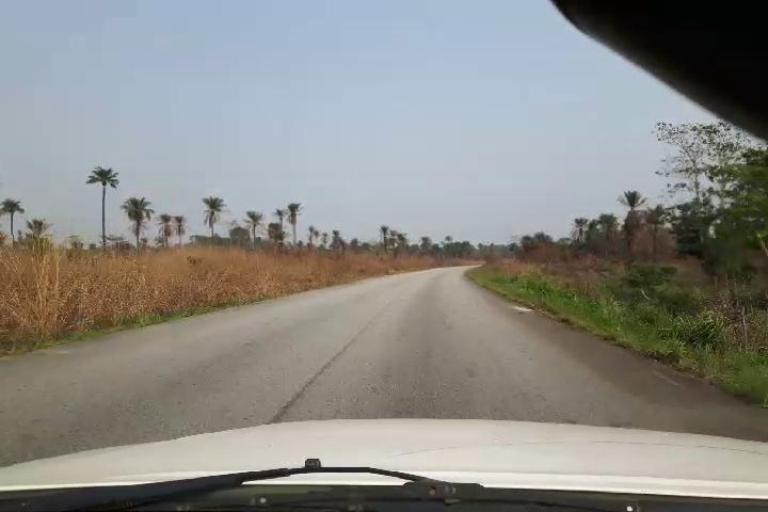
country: SL
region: Southern Province
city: Baiima
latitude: 8.1388
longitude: -11.8973
